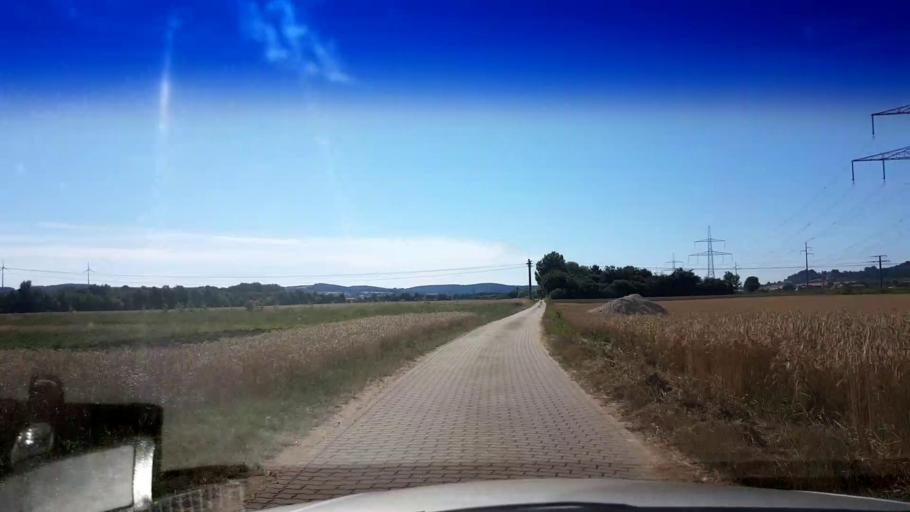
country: DE
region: Bavaria
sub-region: Upper Franconia
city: Oberhaid
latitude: 49.9294
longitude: 10.8013
